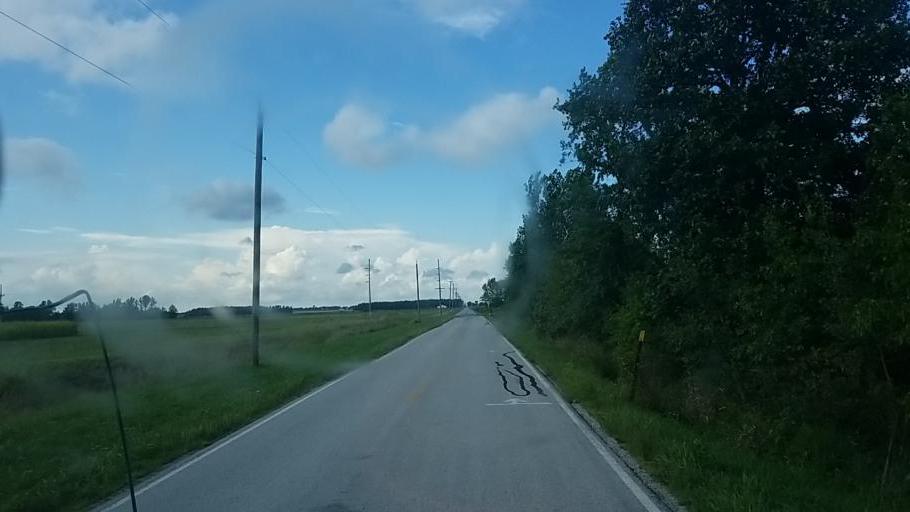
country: US
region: Ohio
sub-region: Hardin County
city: Forest
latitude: 40.7582
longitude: -83.4964
